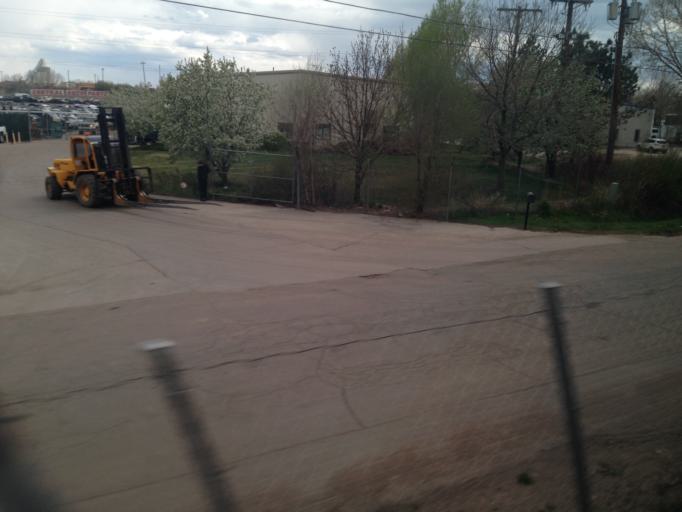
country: US
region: Colorado
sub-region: Adams County
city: Berkley
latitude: 39.8059
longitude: -105.0128
